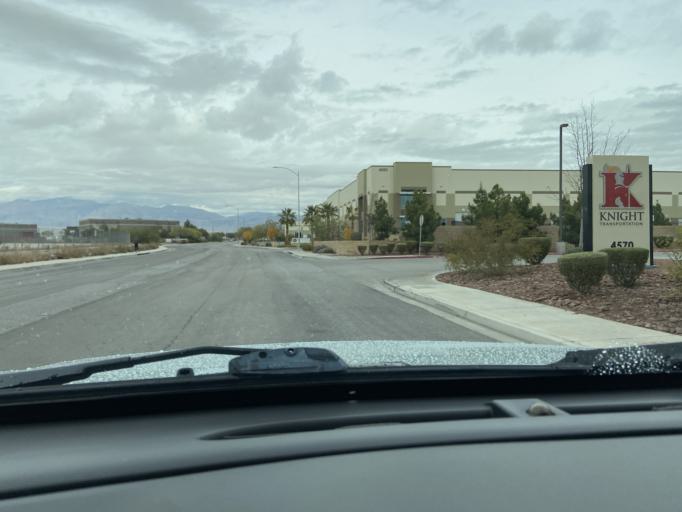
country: US
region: Nevada
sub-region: Clark County
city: North Las Vegas
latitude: 36.2429
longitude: -115.1122
